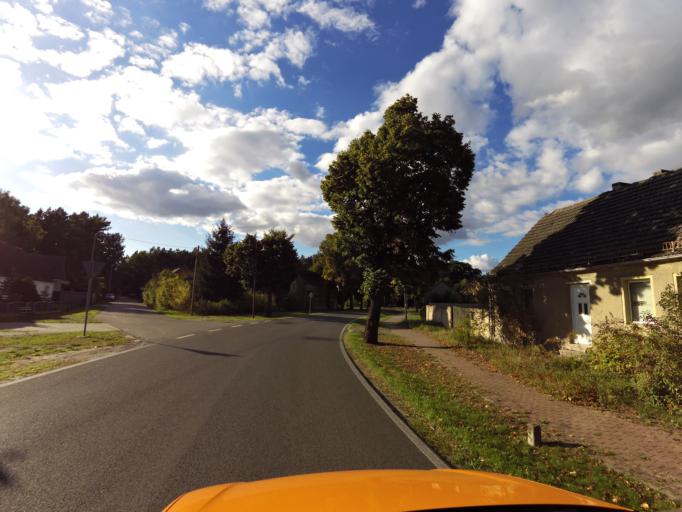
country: DE
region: Brandenburg
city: Trebbin
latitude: 52.1641
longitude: 13.1795
